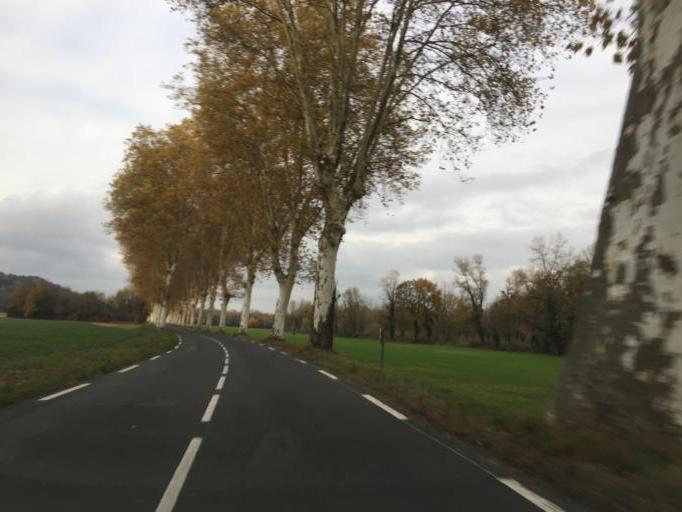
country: FR
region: Rhone-Alpes
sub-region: Departement de l'Ain
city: Chazey-sur-Ain
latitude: 45.9226
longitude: 5.2366
